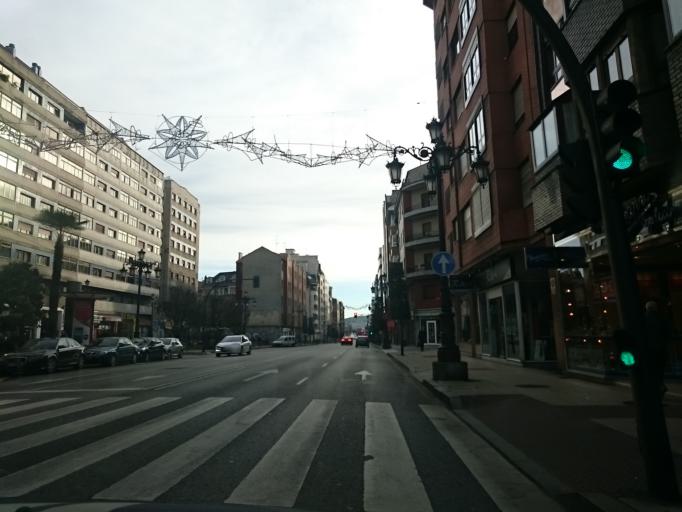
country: ES
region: Asturias
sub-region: Province of Asturias
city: Oviedo
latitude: 43.3623
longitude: -5.8388
